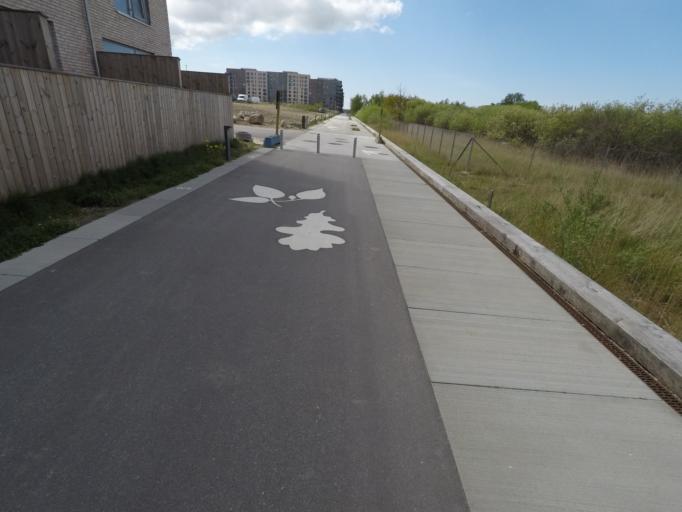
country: DK
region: Capital Region
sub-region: Tarnby Kommune
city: Tarnby
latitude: 55.6231
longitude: 12.5684
